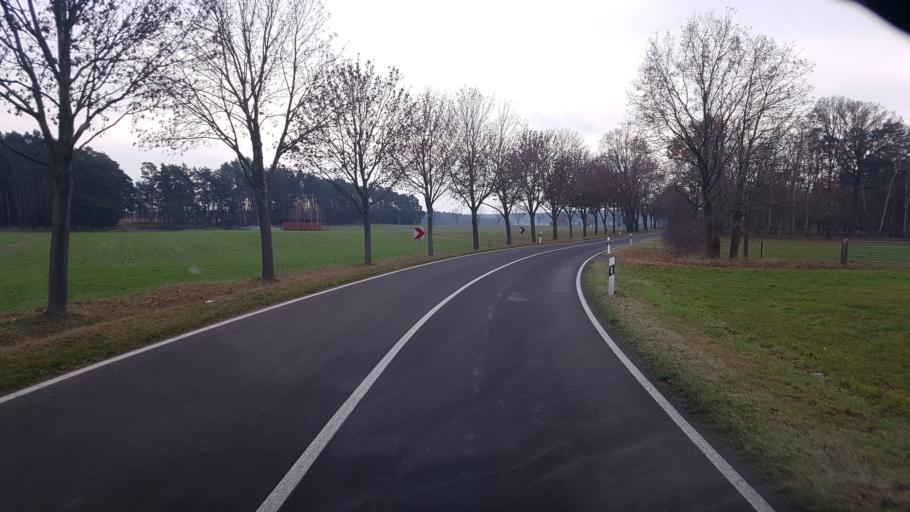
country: DE
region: Brandenburg
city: Schenkendobern
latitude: 51.9417
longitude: 14.6326
